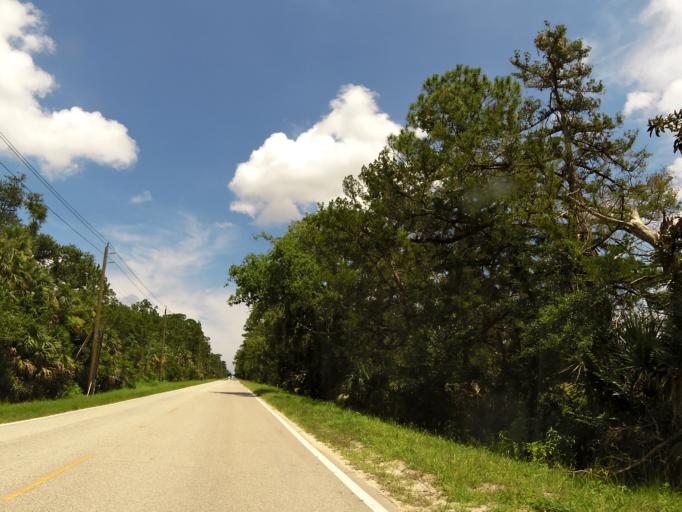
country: US
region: Florida
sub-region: Flagler County
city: Flagler Beach
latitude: 29.4035
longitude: -81.1797
